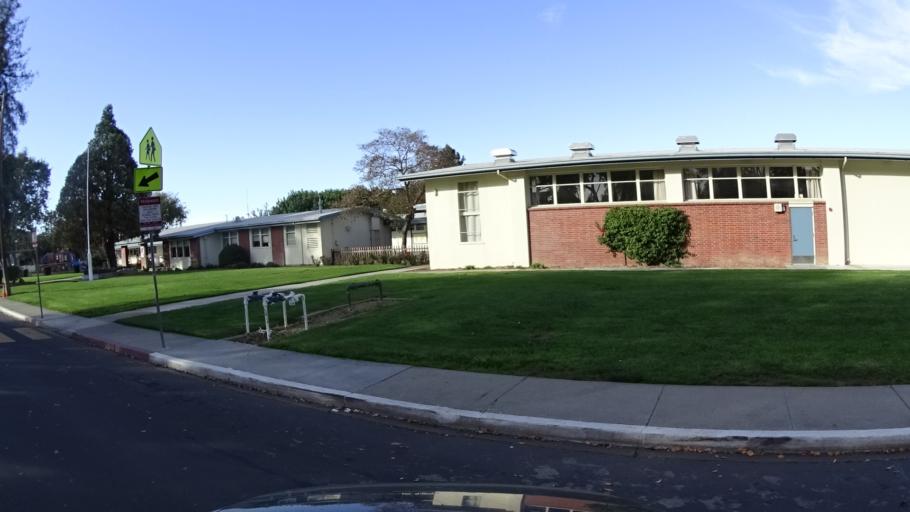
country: US
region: California
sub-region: Santa Clara County
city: Santa Clara
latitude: 37.3571
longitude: -121.9754
